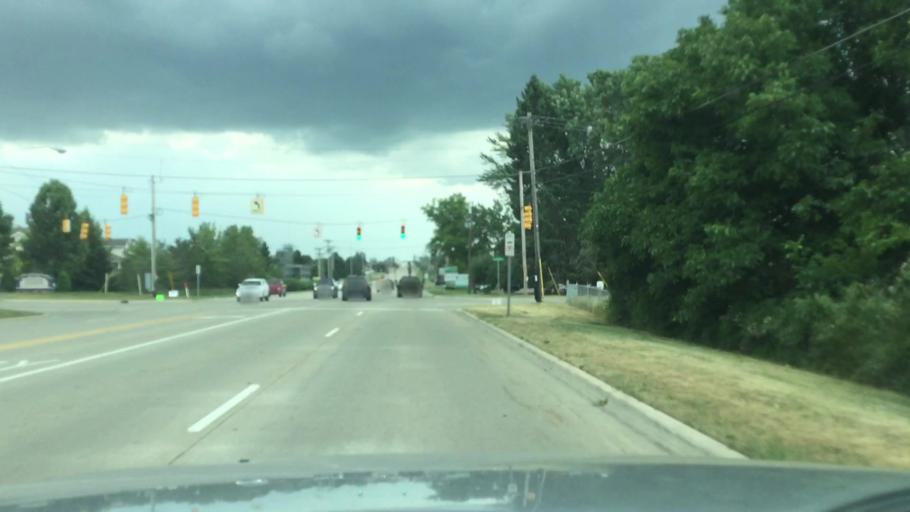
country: US
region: Michigan
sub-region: Genesee County
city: Swartz Creek
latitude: 43.0171
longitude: -83.7732
